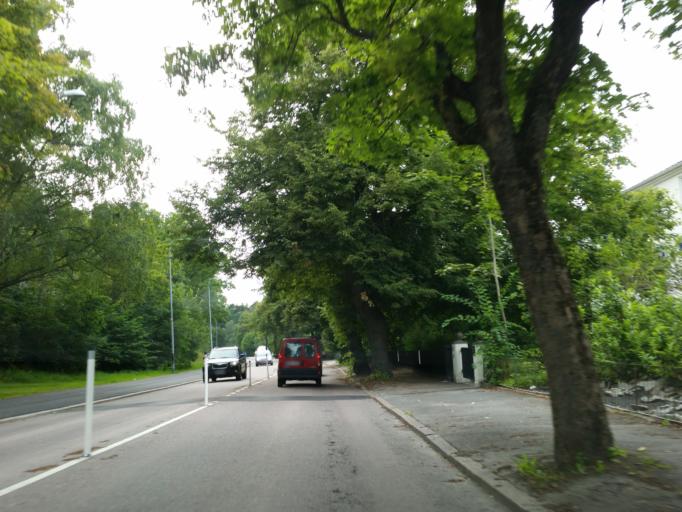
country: SE
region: Stockholm
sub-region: Solna Kommun
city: Rasunda
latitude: 59.3703
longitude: 17.9872
